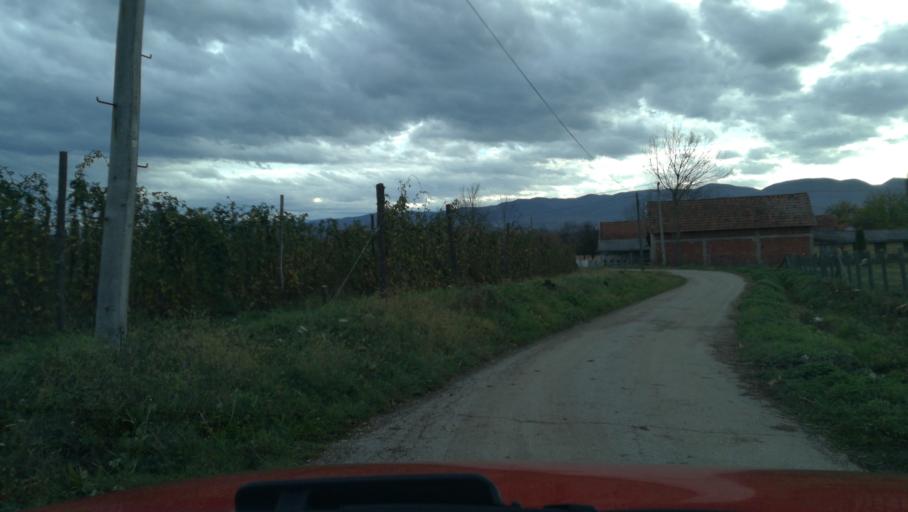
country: RS
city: Prislonica
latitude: 43.9074
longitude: 20.4306
